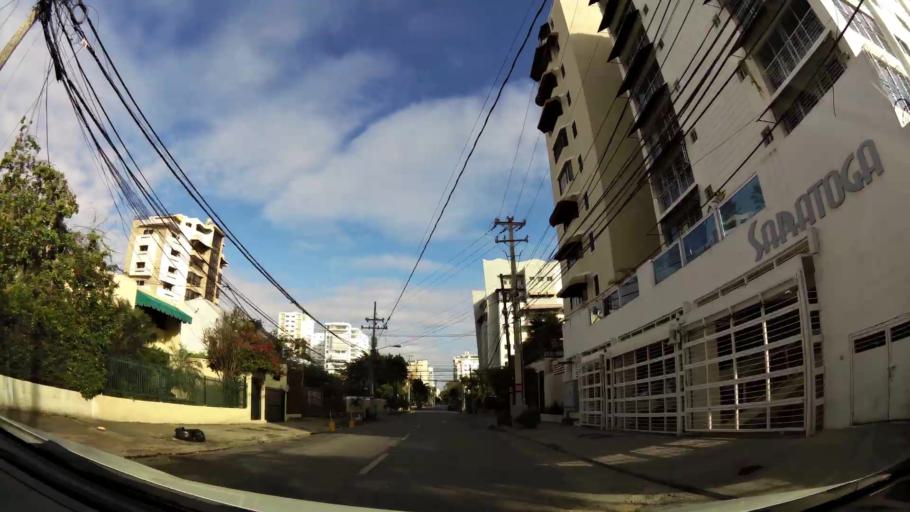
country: DO
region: Nacional
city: La Julia
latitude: 18.4660
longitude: -69.9330
